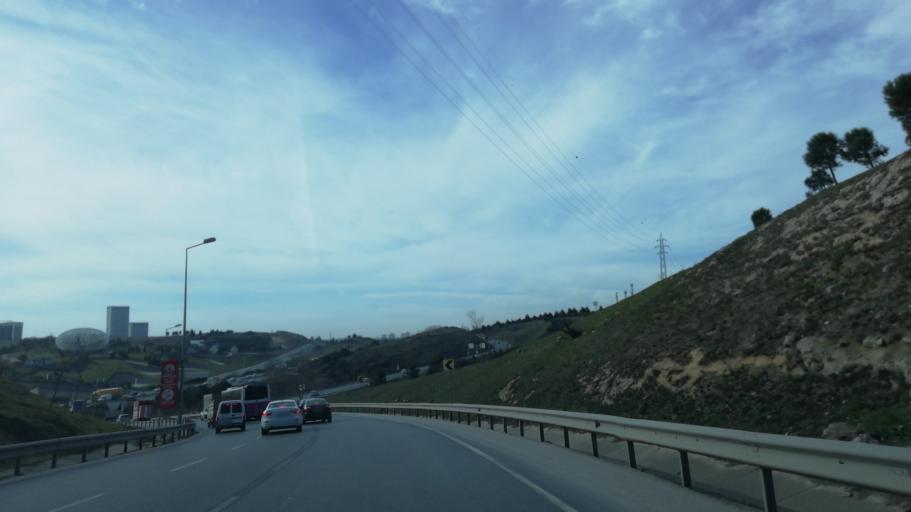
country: TR
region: Istanbul
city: Basaksehir
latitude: 41.0636
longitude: 28.7754
